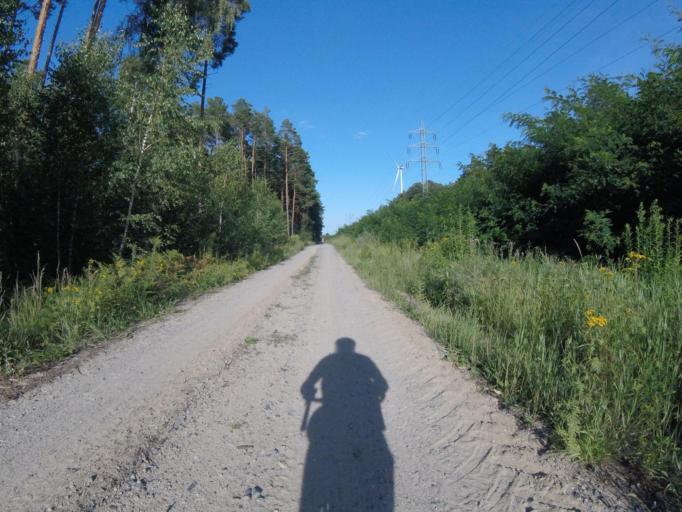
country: DE
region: Brandenburg
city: Erkner
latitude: 52.3362
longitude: 13.7433
